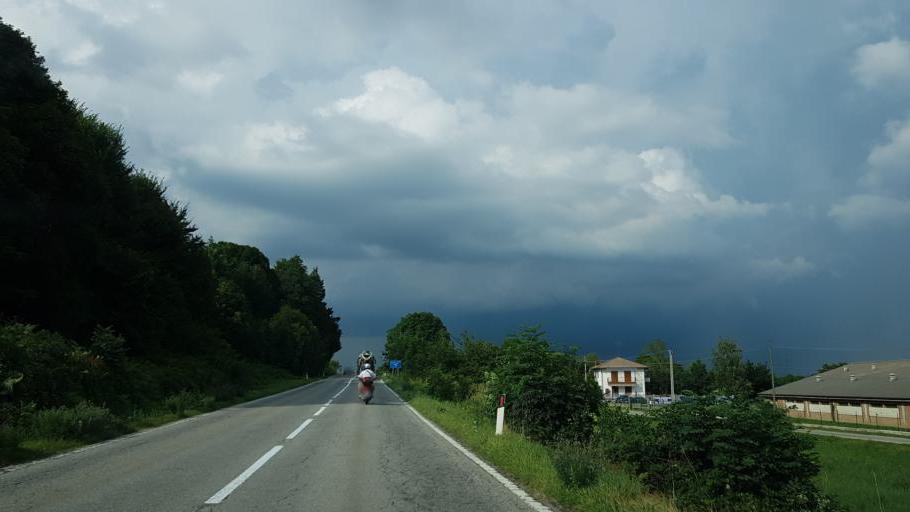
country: IT
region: Piedmont
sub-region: Provincia di Cuneo
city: Vignolo
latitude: 44.3522
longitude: 7.4774
